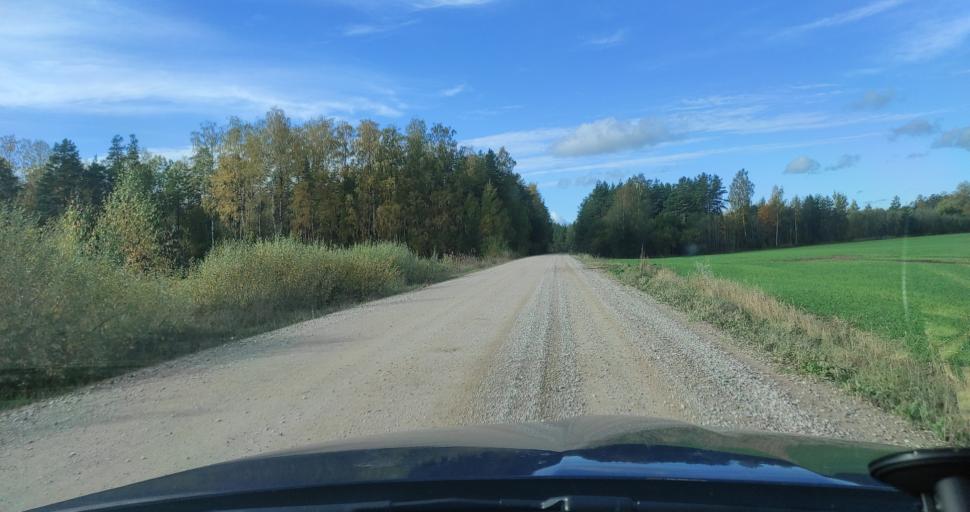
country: LV
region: Jaunpils
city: Jaunpils
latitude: 56.8301
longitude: 23.0091
